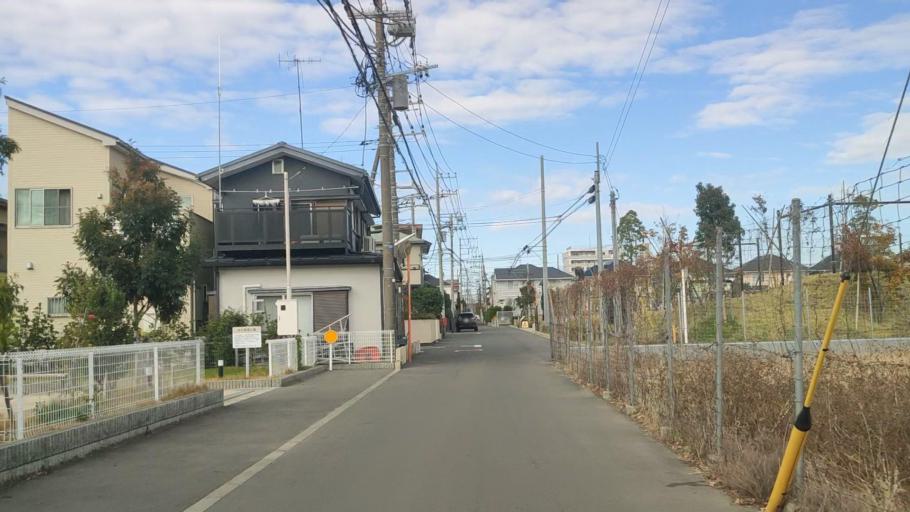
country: JP
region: Kanagawa
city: Minami-rinkan
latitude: 35.4882
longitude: 139.4383
